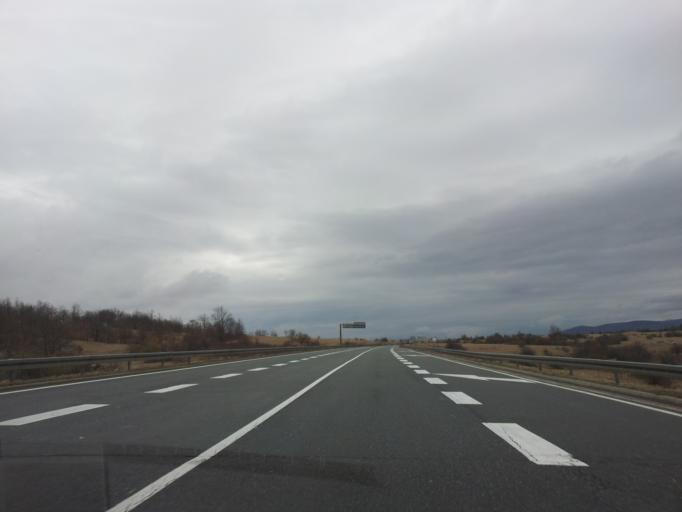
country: HR
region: Zadarska
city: Gracac
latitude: 44.5102
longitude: 15.7456
